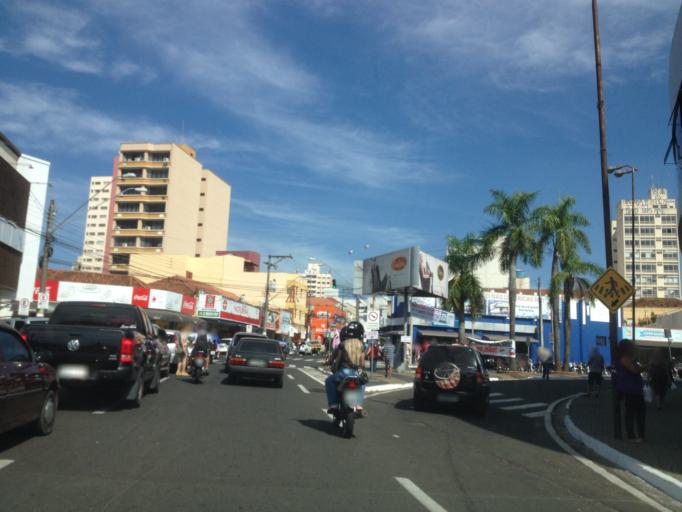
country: BR
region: Sao Paulo
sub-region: Marilia
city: Marilia
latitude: -22.2171
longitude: -49.9468
